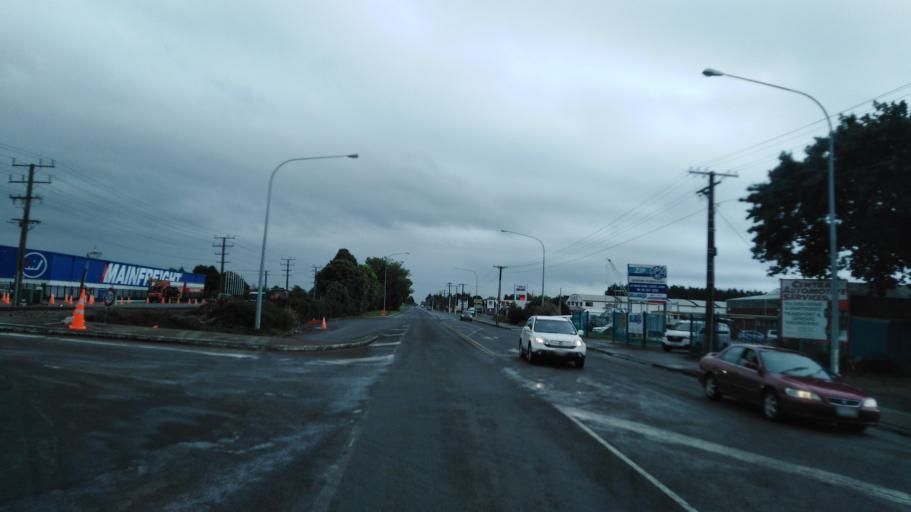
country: NZ
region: Manawatu-Wanganui
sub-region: Horowhenua District
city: Levin
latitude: -40.6359
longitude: 175.2729
